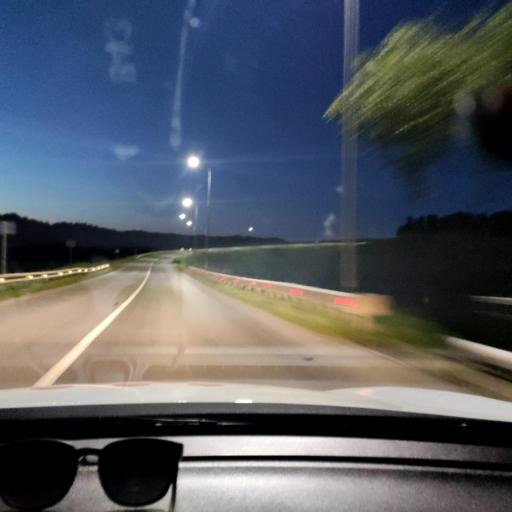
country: RU
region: Tatarstan
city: Rybnaya Sloboda
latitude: 55.4750
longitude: 50.0264
